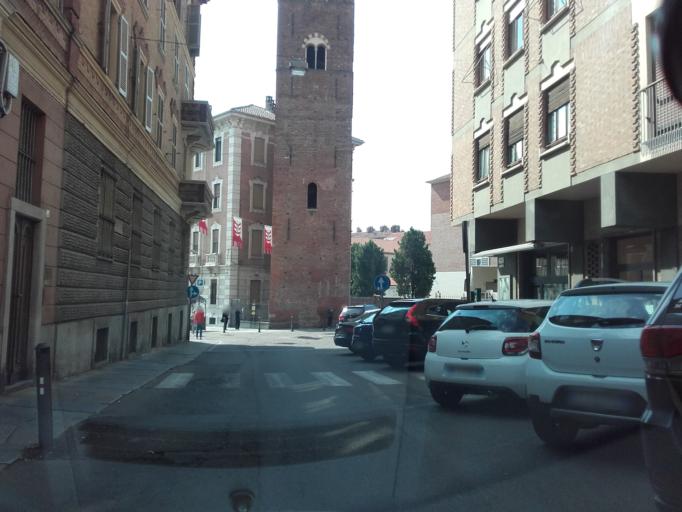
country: IT
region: Piedmont
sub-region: Provincia di Asti
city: Asti
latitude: 44.9013
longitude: 8.2043
